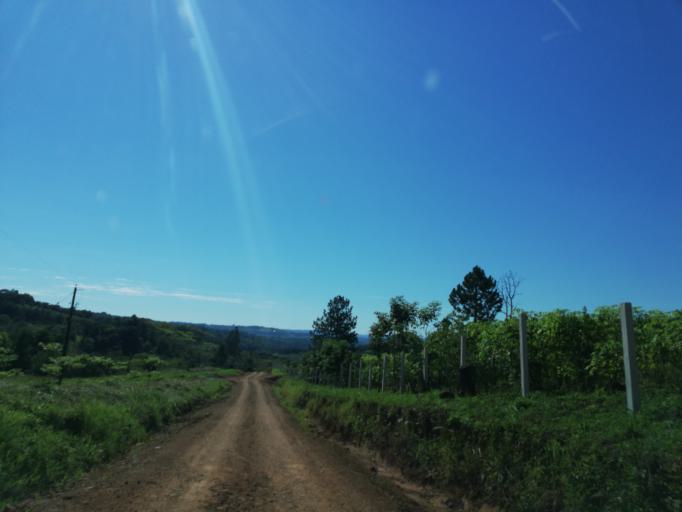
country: AR
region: Misiones
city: Dos de Mayo
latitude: -27.0731
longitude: -54.3967
